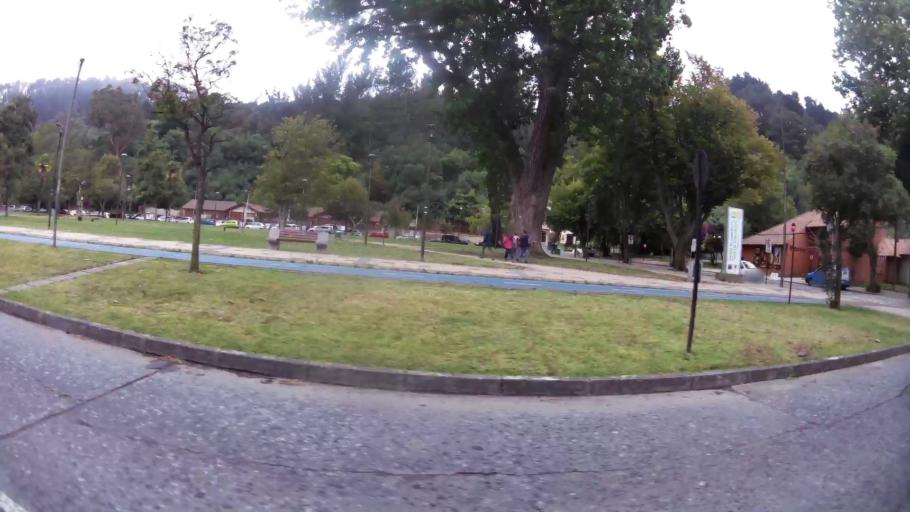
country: CL
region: Biobio
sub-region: Provincia de Concepcion
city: Concepcion
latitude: -36.8334
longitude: -73.0498
